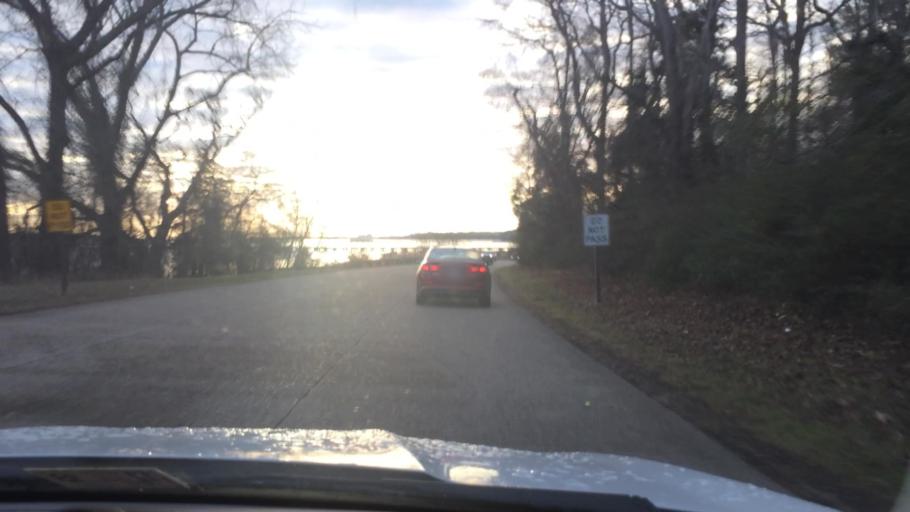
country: US
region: Virginia
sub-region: York County
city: Yorktown
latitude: 37.2585
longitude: -76.5445
